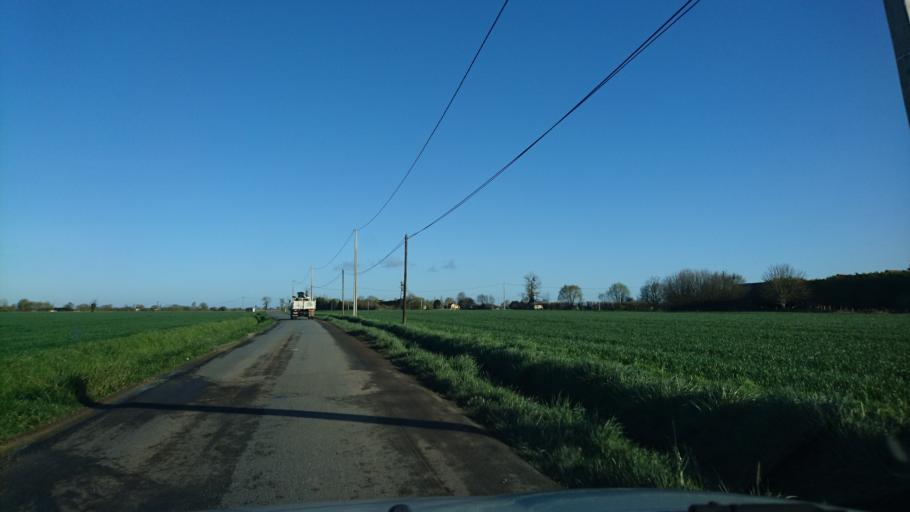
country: FR
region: Brittany
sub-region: Departement d'Ille-et-Vilaine
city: Cherrueix
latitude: 48.5848
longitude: -1.7167
